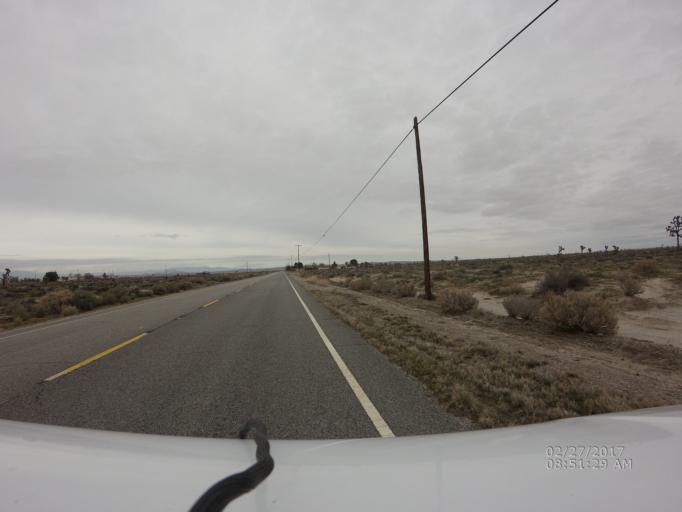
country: US
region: California
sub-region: Los Angeles County
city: Lancaster
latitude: 34.7497
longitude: -118.0771
